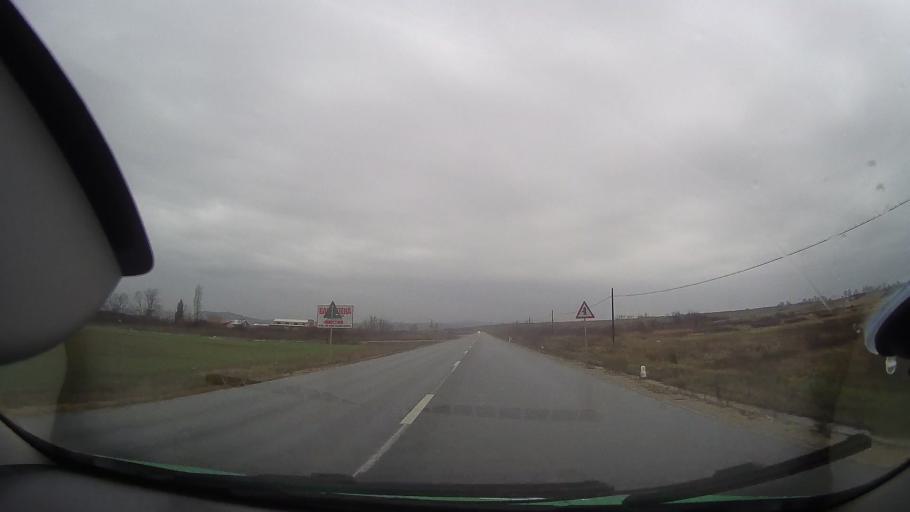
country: RO
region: Bihor
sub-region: Municipiul Beius
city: Beius
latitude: 46.6758
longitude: 22.3225
